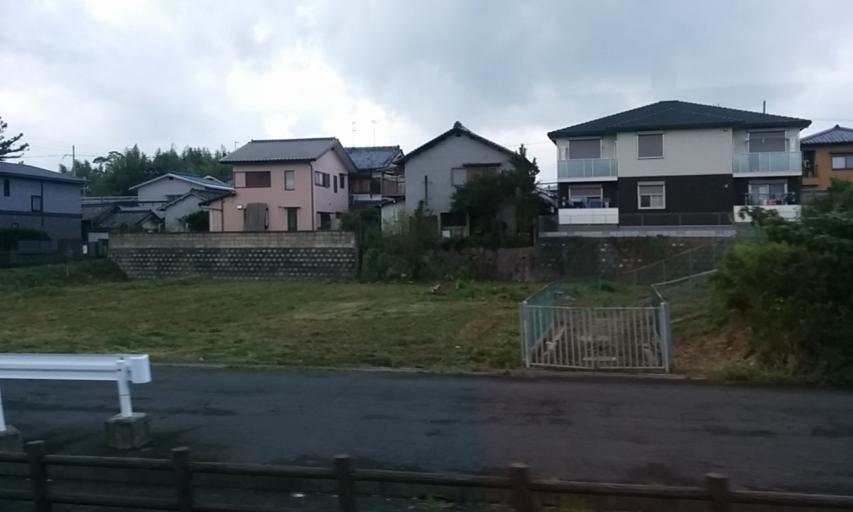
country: JP
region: Nara
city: Nara-shi
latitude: 34.6654
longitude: 135.7837
